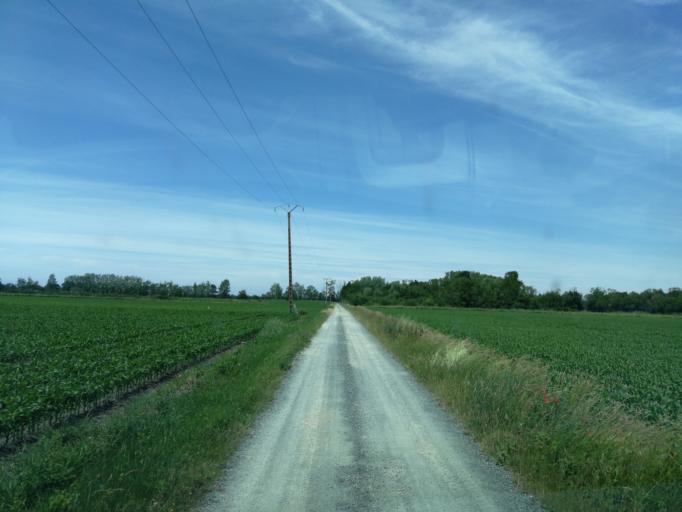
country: FR
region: Poitou-Charentes
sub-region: Departement de la Charente-Maritime
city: Marans
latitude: 46.3645
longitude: -0.9567
